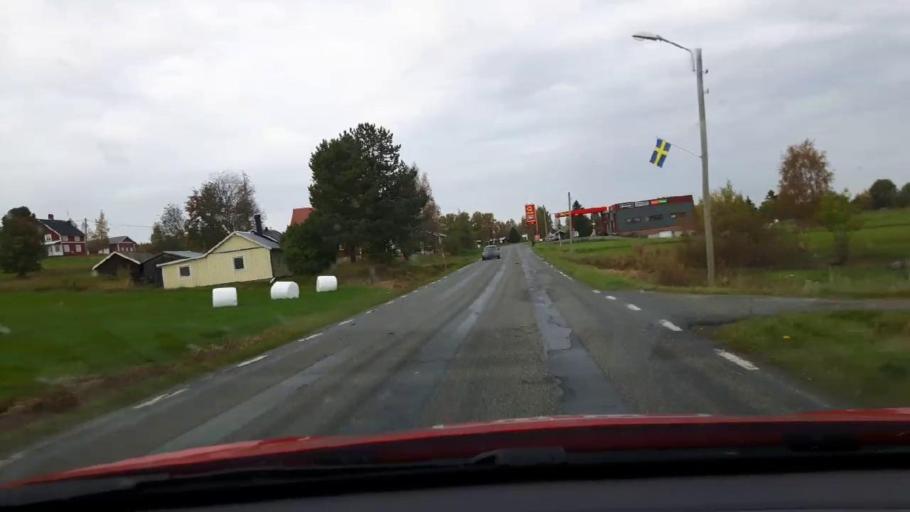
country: SE
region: Jaemtland
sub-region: Bergs Kommun
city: Hoverberg
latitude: 62.8371
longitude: 14.3843
